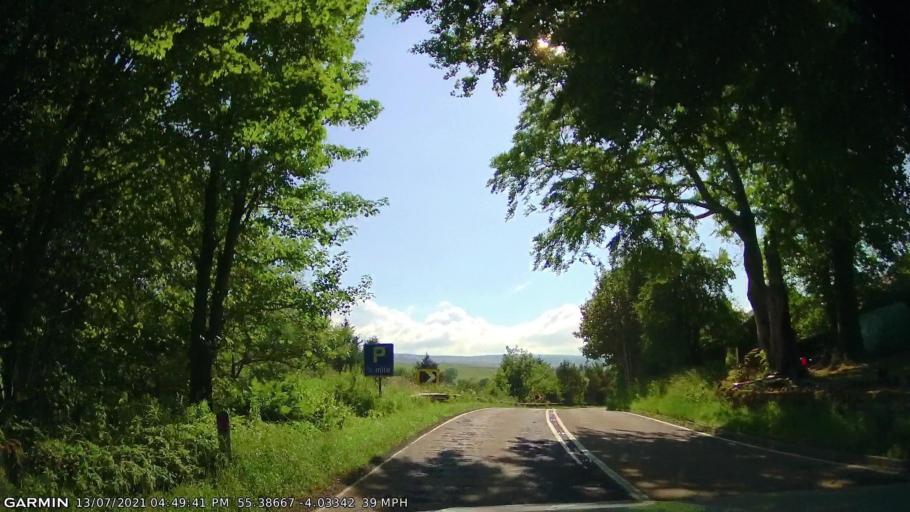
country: GB
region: Scotland
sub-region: Dumfries and Galloway
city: Kirkconnel
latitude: 55.3867
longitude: -4.0334
